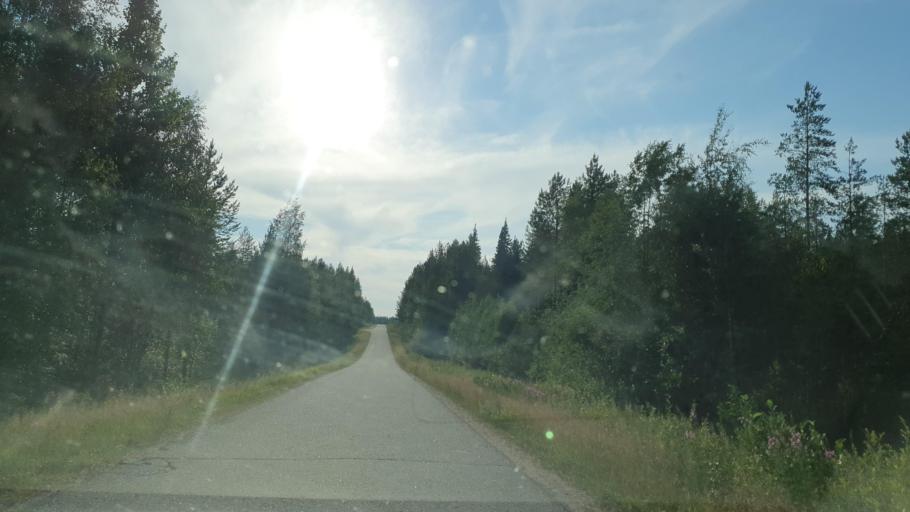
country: FI
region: Kainuu
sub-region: Kehys-Kainuu
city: Kuhmo
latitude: 64.2806
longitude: 29.4146
